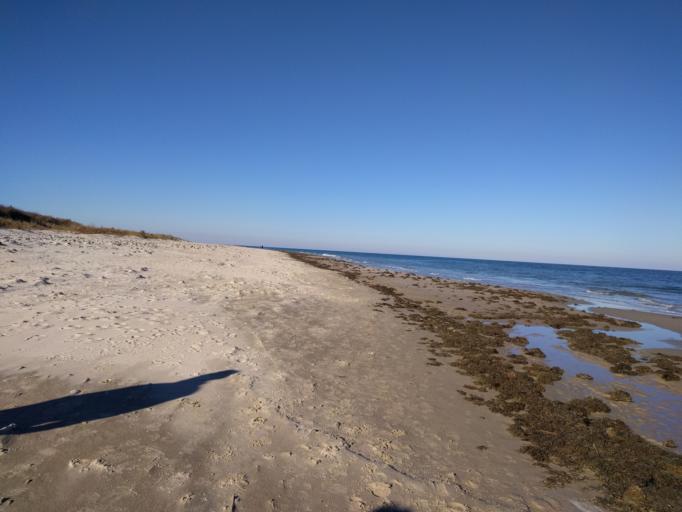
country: US
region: Virginia
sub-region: City of Hampton
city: East Hampton
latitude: 37.0873
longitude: -76.2708
